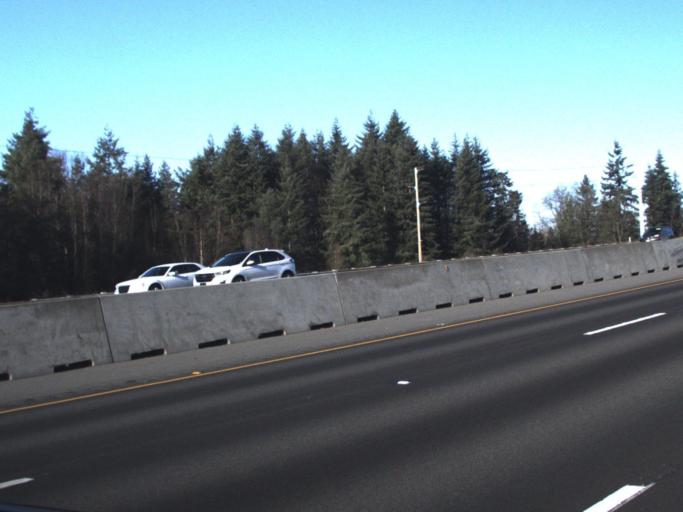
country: US
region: Washington
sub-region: Snohomish County
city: Smokey Point
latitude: 48.1212
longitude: -122.1851
